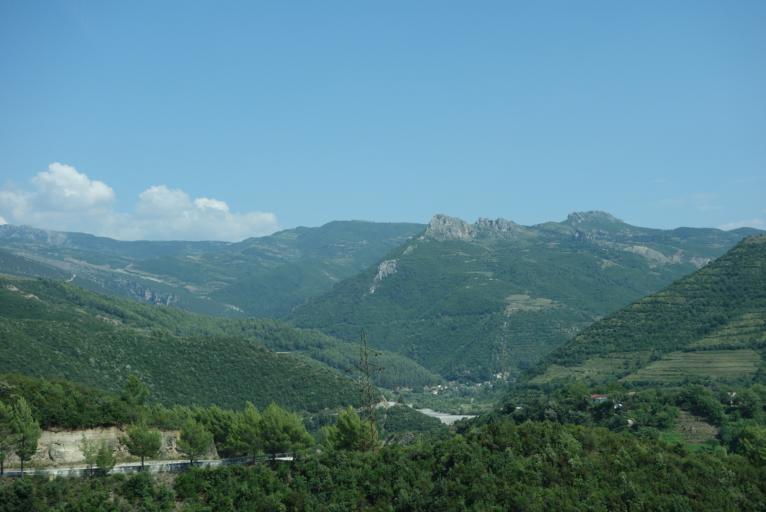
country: AL
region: Berat
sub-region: Rrethi i Skraparit
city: Bogove
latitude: 40.5814
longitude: 20.1272
